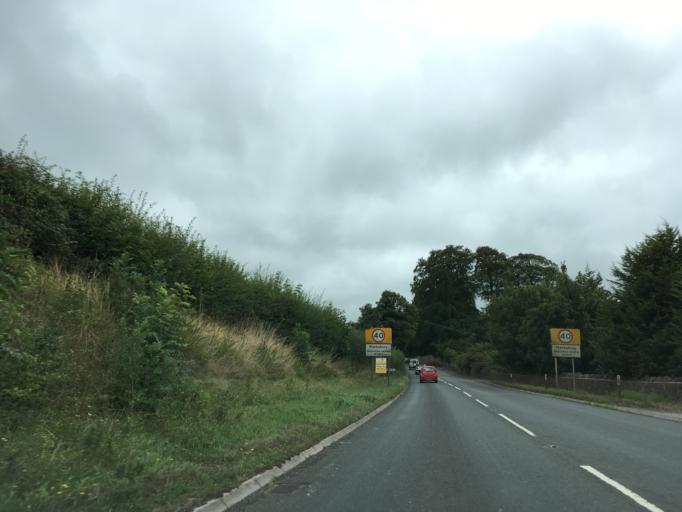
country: GB
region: England
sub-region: Bath and North East Somerset
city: Compton Dando
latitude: 51.3652
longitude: -2.4787
